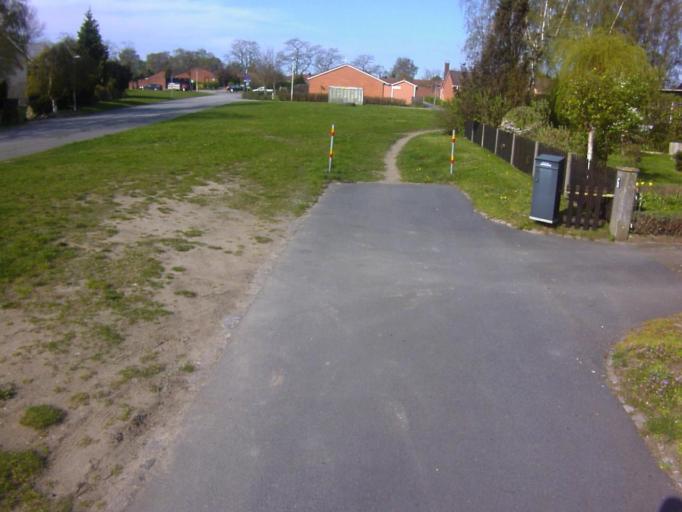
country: SE
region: Skane
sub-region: Kavlinge Kommun
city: Loddekopinge
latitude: 55.7579
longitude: 13.0134
